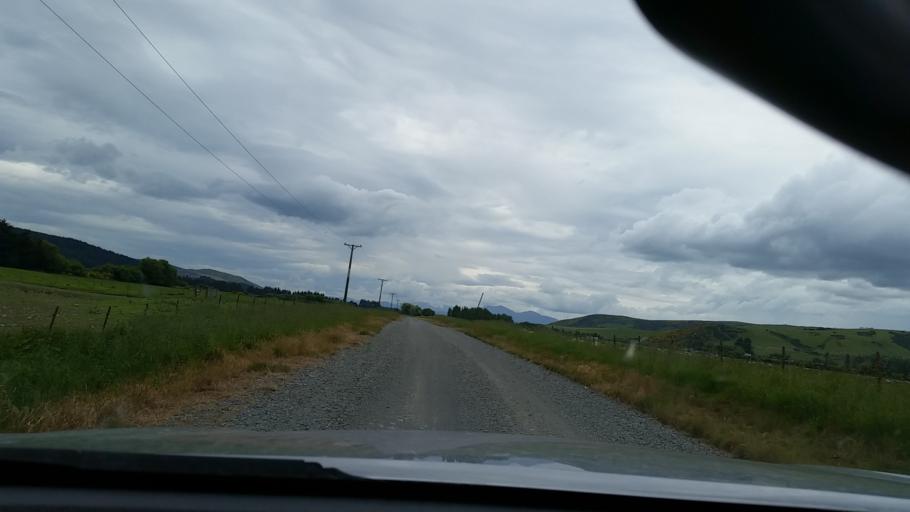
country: NZ
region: Southland
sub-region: Southland District
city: Winton
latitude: -45.8440
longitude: 168.1407
